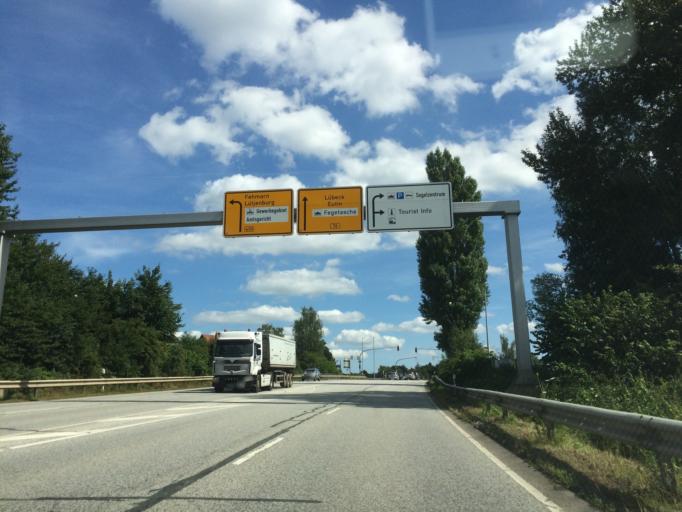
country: DE
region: Schleswig-Holstein
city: Ploen
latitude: 54.1621
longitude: 10.4250
